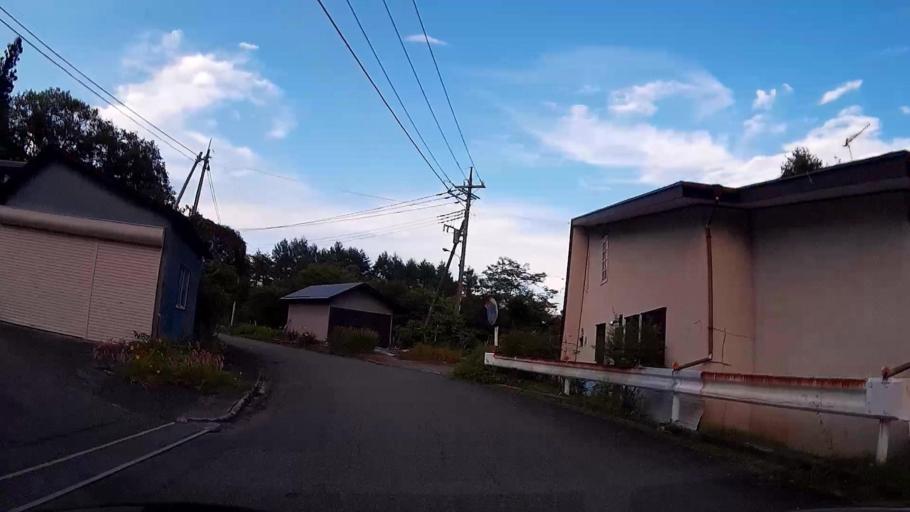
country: JP
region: Gunma
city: Nakanojomachi
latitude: 36.6251
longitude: 138.6219
